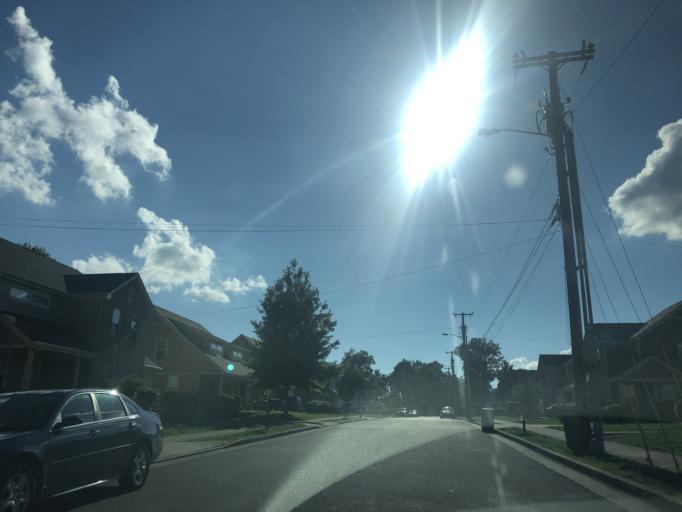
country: US
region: Tennessee
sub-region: Davidson County
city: Nashville
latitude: 36.1801
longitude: -86.7657
